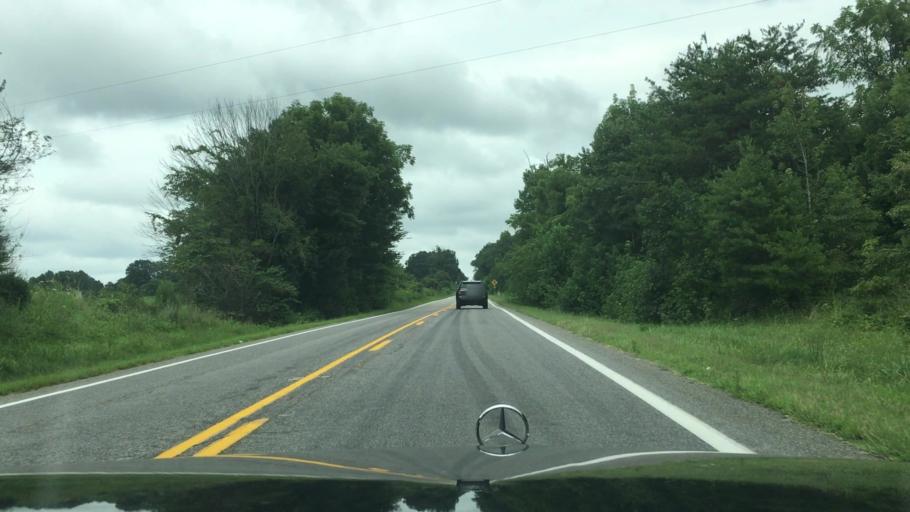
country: US
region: Virginia
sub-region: Prince Edward County
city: Farmville
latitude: 37.2739
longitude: -78.2594
